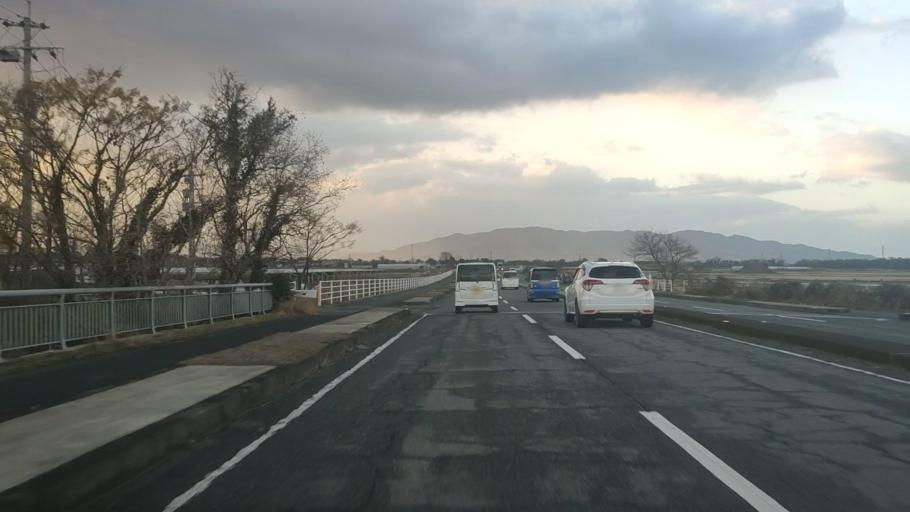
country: JP
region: Kumamoto
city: Kumamoto
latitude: 32.7527
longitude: 130.7066
